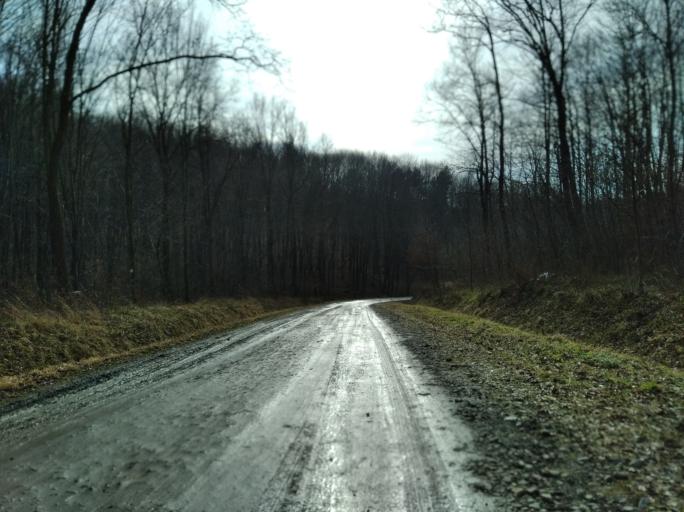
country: PL
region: Subcarpathian Voivodeship
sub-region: Powiat brzozowski
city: Gorki
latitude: 49.6391
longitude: 22.0594
